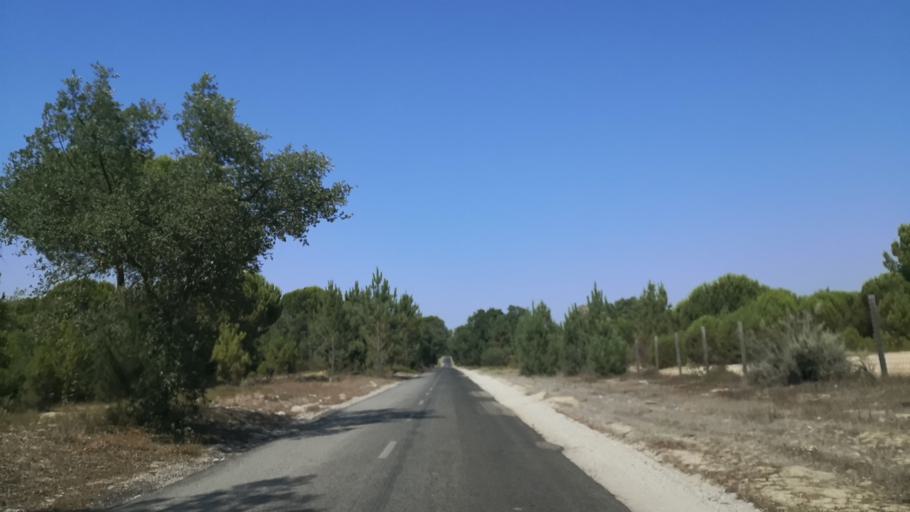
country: PT
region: Santarem
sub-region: Benavente
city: Poceirao
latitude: 38.7255
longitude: -8.7055
